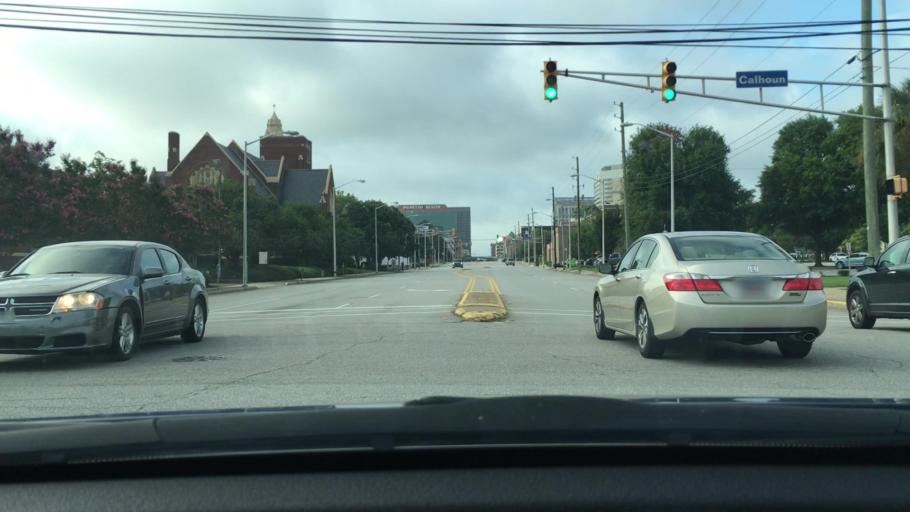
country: US
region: South Carolina
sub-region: Richland County
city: Columbia
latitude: 34.0125
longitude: -81.0367
